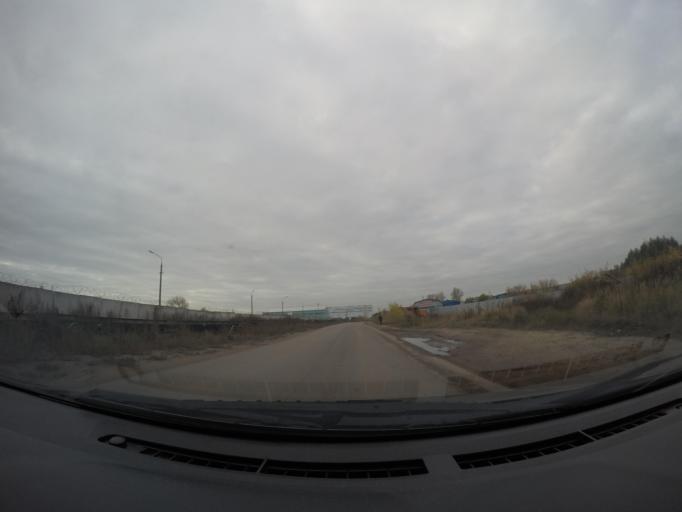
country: RU
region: Moskovskaya
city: Staraya Kupavna
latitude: 55.7943
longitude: 38.1835
